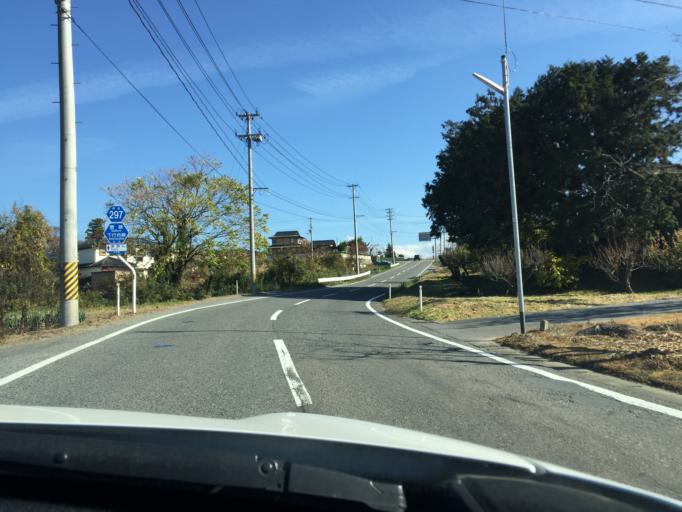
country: JP
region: Fukushima
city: Koriyama
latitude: 37.3833
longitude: 140.4126
